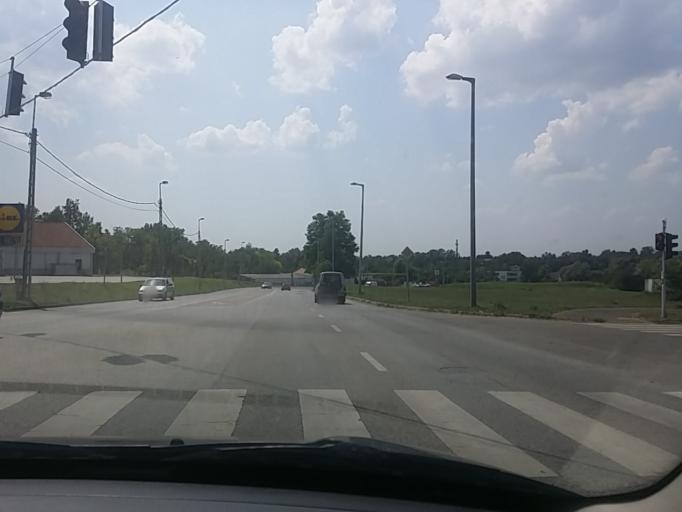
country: HU
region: Tolna
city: Dombovar
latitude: 46.3884
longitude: 18.1429
